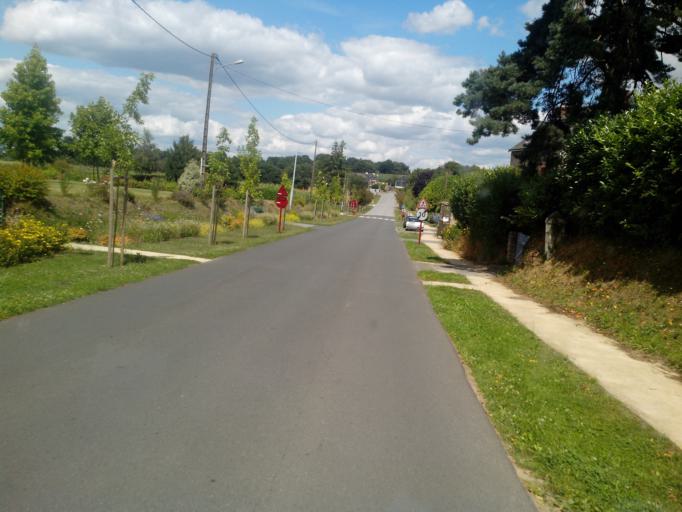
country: FR
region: Brittany
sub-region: Departement du Morbihan
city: Guegon
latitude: 47.9408
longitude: -2.5624
